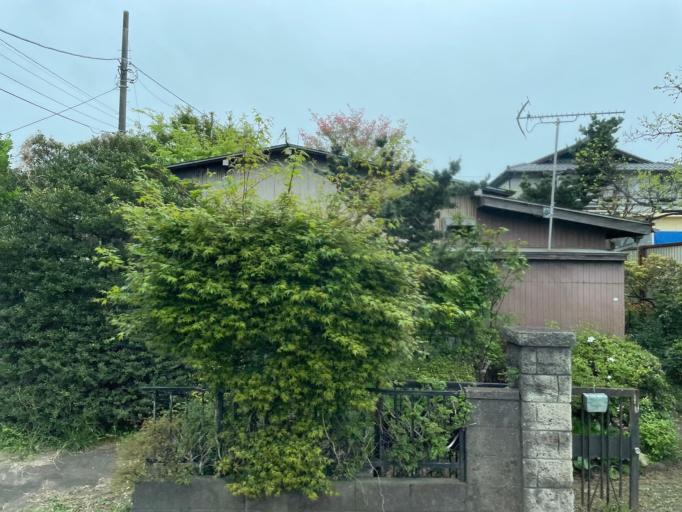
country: JP
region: Saitama
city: Saitama
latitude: 35.9042
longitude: 139.7029
